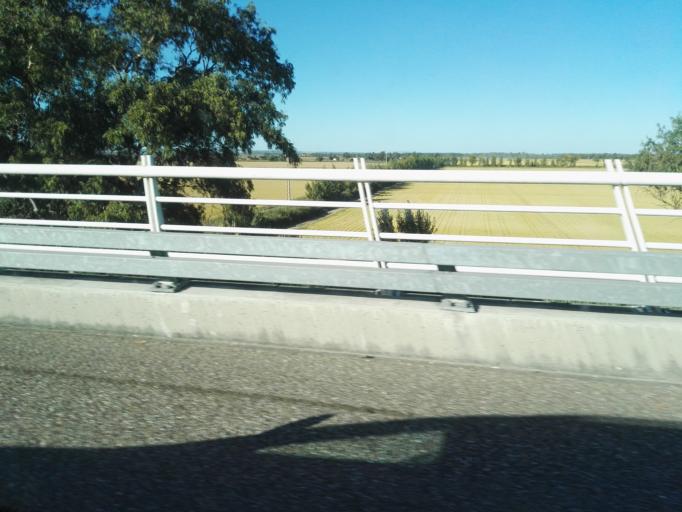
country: PT
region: Santarem
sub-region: Benavente
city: Samora Correia
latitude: 38.9686
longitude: -8.8673
